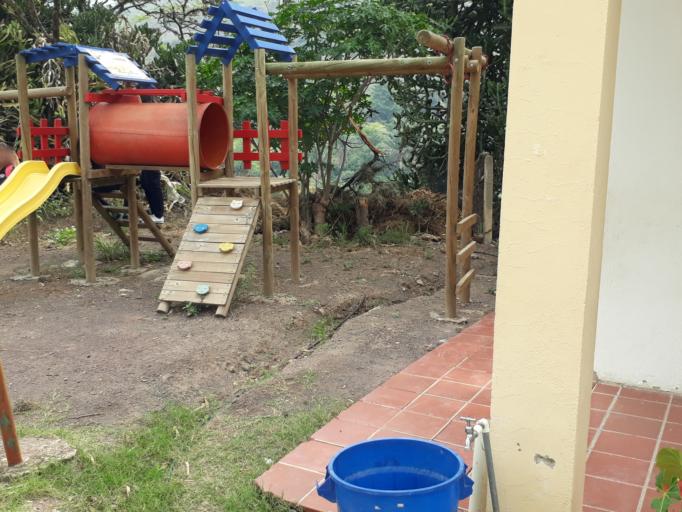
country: CO
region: Boyaca
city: Soata
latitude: 6.3243
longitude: -72.6498
